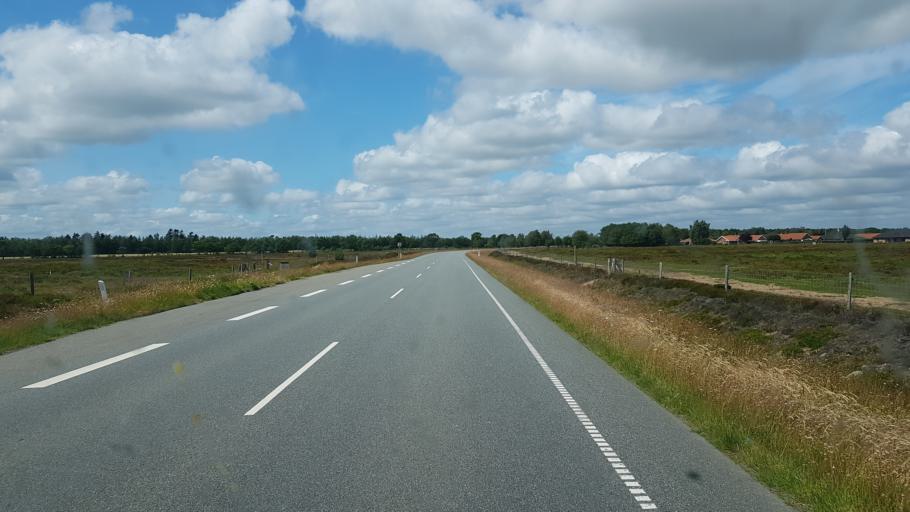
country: DK
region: South Denmark
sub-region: Billund Kommune
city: Grindsted
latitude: 55.7452
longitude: 8.9088
